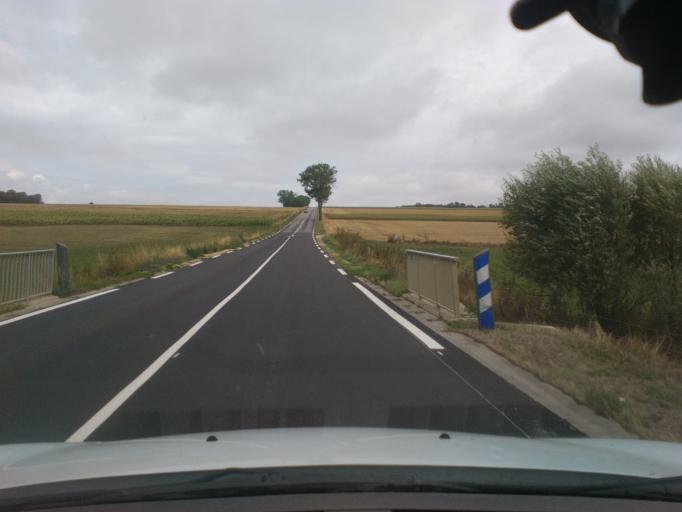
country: FR
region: Lorraine
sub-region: Departement de Meurthe-et-Moselle
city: Vezelise
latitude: 48.4351
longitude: 6.1252
